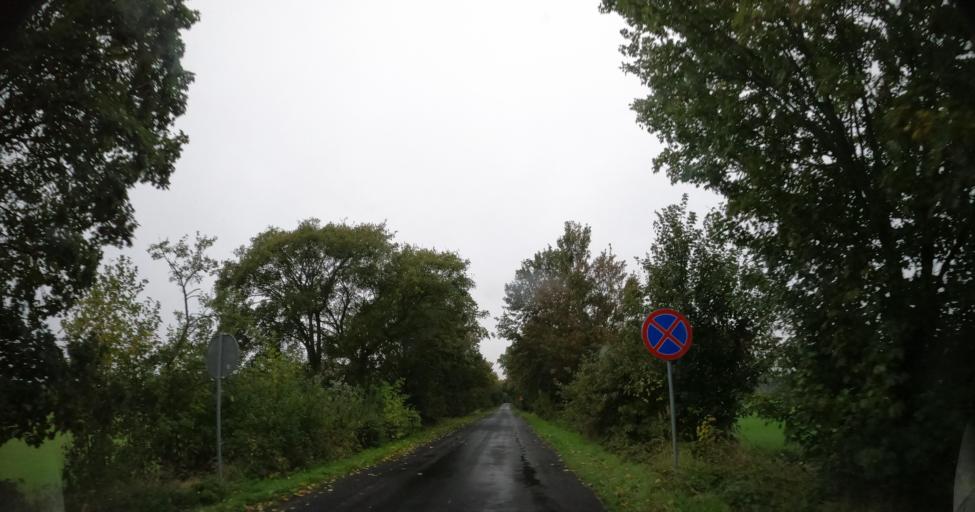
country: PL
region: West Pomeranian Voivodeship
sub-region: Powiat pyrzycki
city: Kozielice
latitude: 53.0522
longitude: 14.7454
